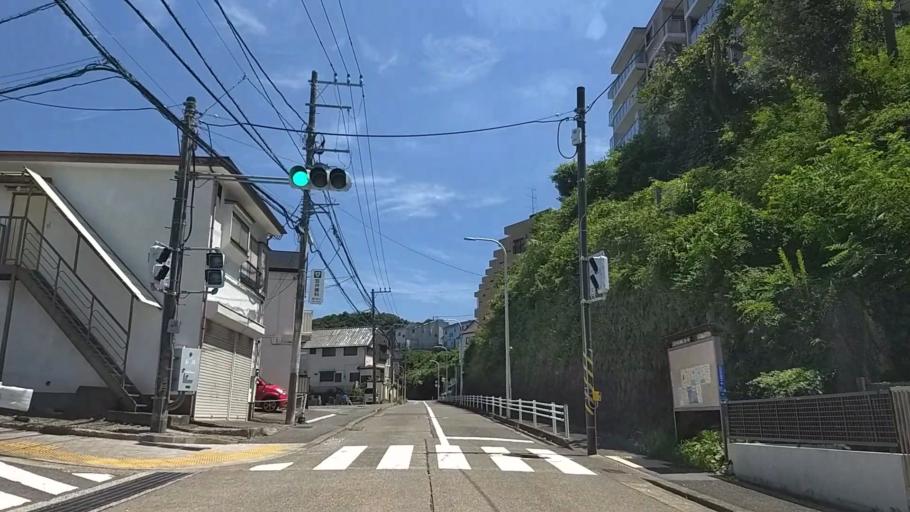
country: JP
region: Kanagawa
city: Zushi
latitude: 35.3061
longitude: 139.5962
